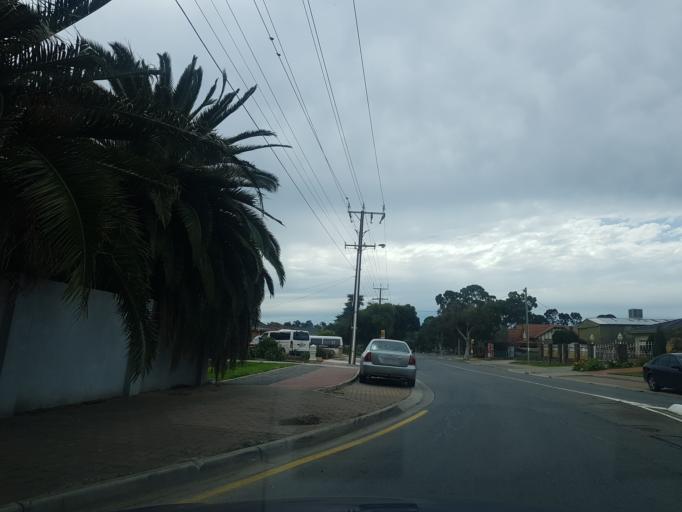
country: AU
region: South Australia
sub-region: Campbelltown
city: Paradise
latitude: -34.8729
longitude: 138.6830
